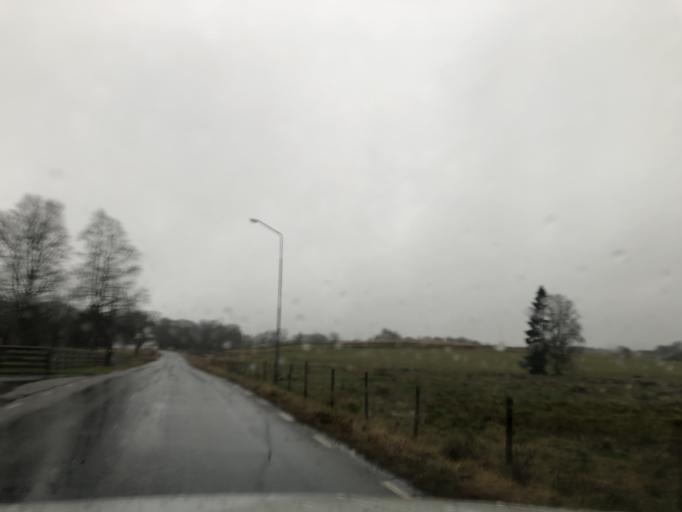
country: SE
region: Vaestra Goetaland
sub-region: Ulricehamns Kommun
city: Ulricehamn
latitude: 57.8295
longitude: 13.5325
